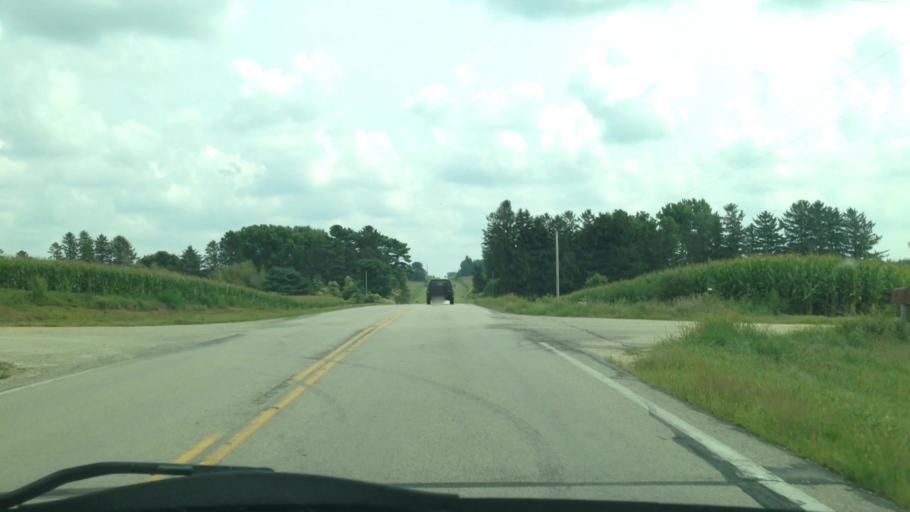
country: US
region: Minnesota
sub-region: Olmsted County
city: Rochester
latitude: 44.1369
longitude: -92.3997
